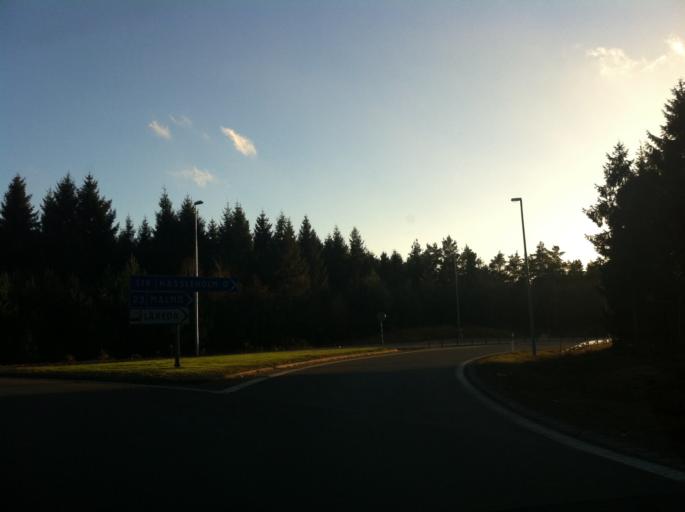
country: SE
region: Skane
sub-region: Hassleholms Kommun
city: Hastveda
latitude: 56.1947
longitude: 13.9000
